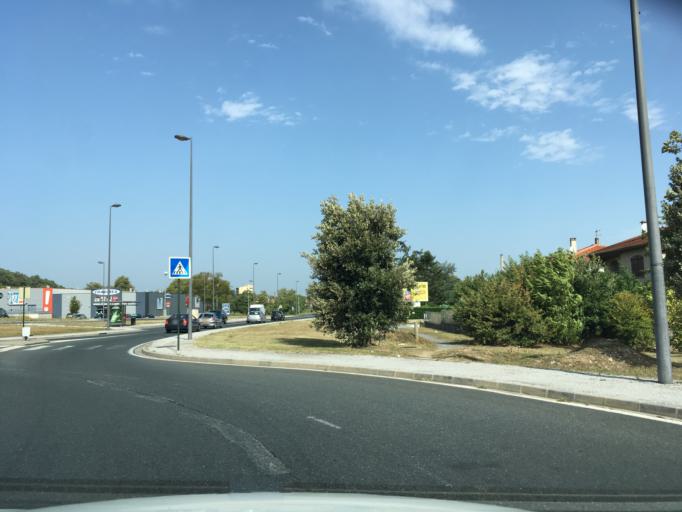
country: FR
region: Midi-Pyrenees
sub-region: Departement du Tarn
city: Castres
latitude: 43.5926
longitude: 2.2668
